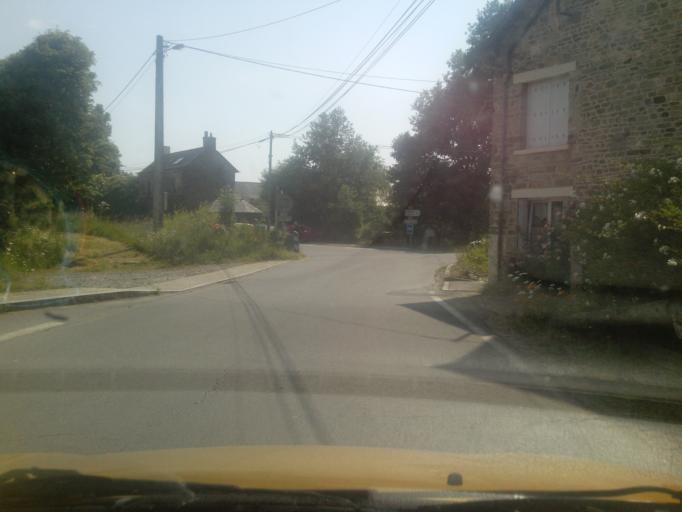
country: FR
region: Brittany
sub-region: Departement d'Ille-et-Vilaine
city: Saint-Medard-sur-Ille
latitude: 48.2476
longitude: -1.6688
